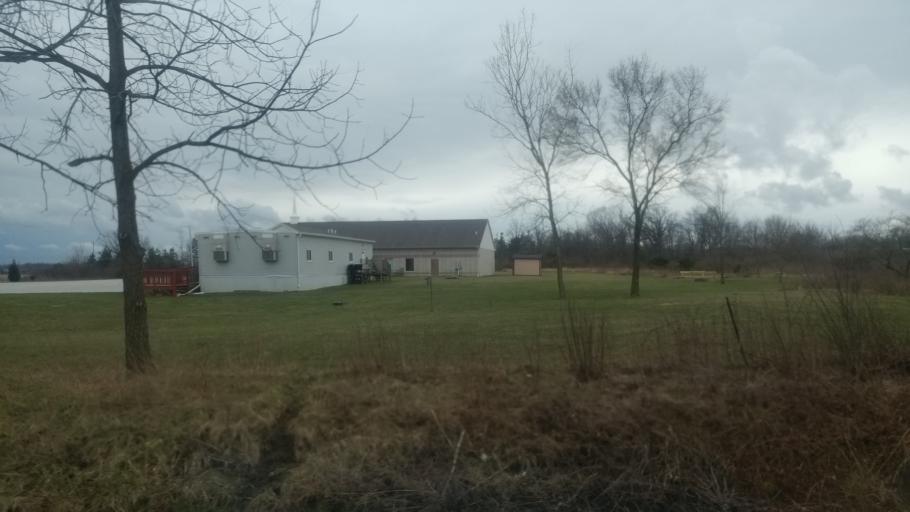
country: US
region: Ohio
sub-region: Wood County
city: Bowling Green
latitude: 41.3636
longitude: -83.6265
